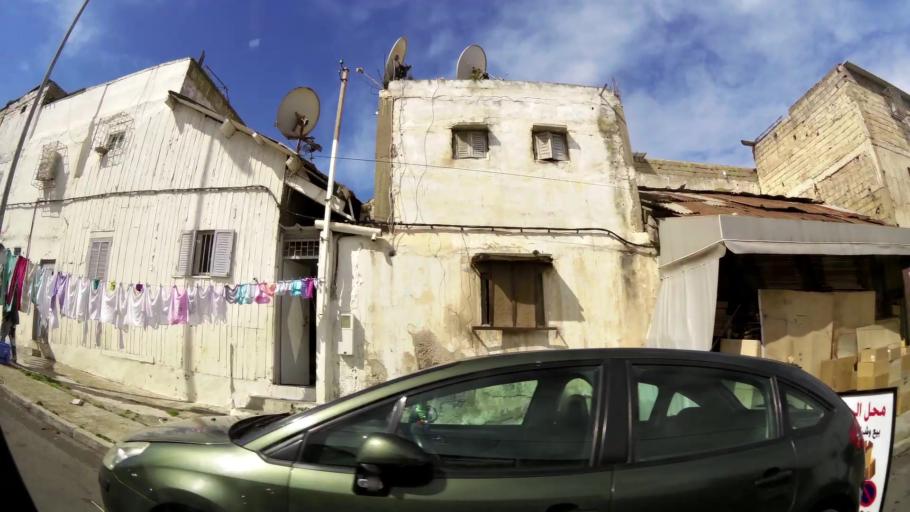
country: MA
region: Grand Casablanca
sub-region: Casablanca
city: Casablanca
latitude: 33.5847
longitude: -7.5926
